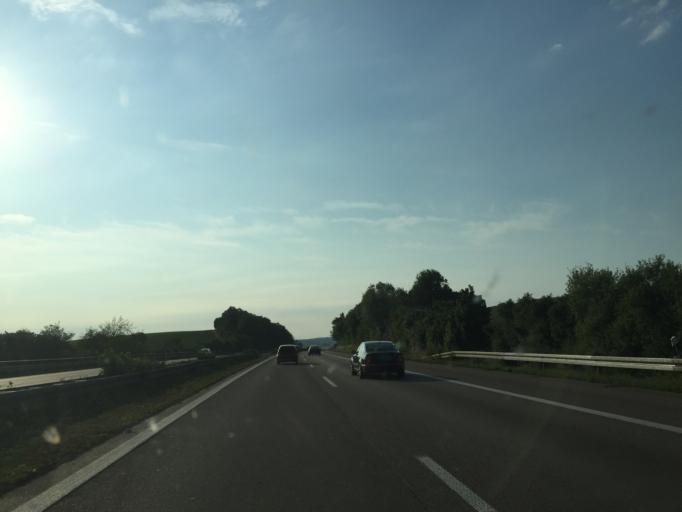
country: DE
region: Baden-Wuerttemberg
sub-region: Regierungsbezirk Stuttgart
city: Bad Rappenau
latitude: 49.2007
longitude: 9.0892
